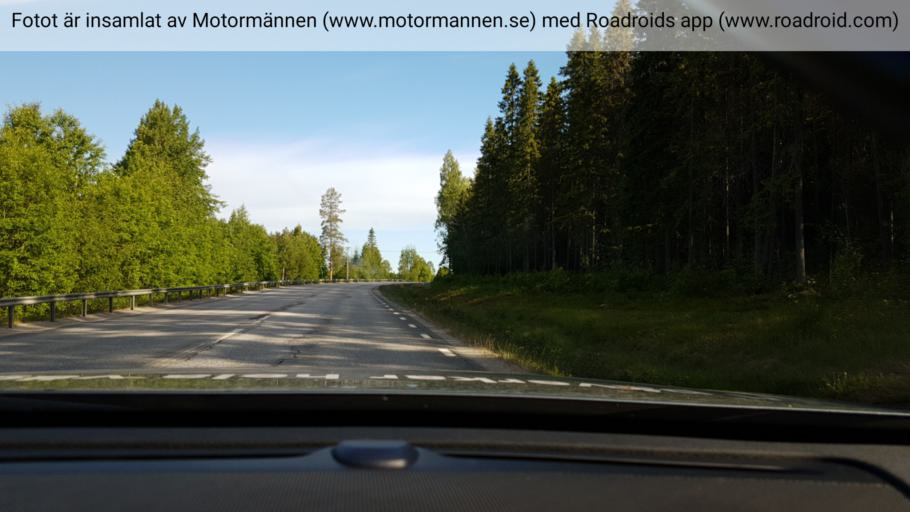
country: SE
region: Vaesterbotten
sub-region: Vannas Kommun
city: Vaennaes
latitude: 63.9763
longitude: 19.7325
